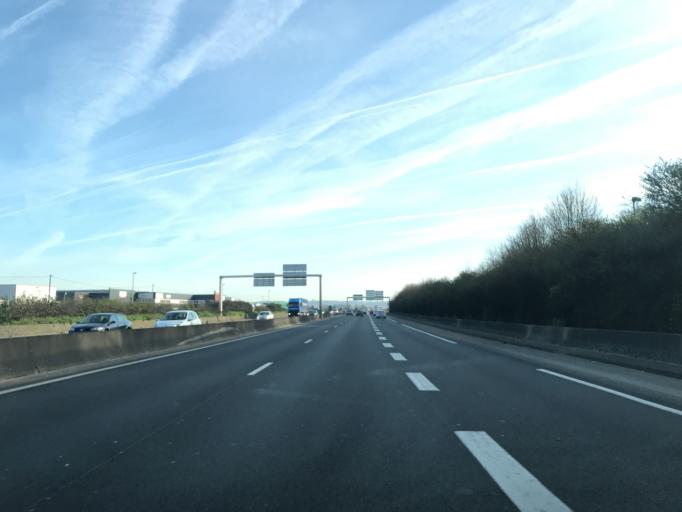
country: FR
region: Haute-Normandie
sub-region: Departement de la Seine-Maritime
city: Le Grand-Quevilly
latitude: 49.4037
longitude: 1.0342
